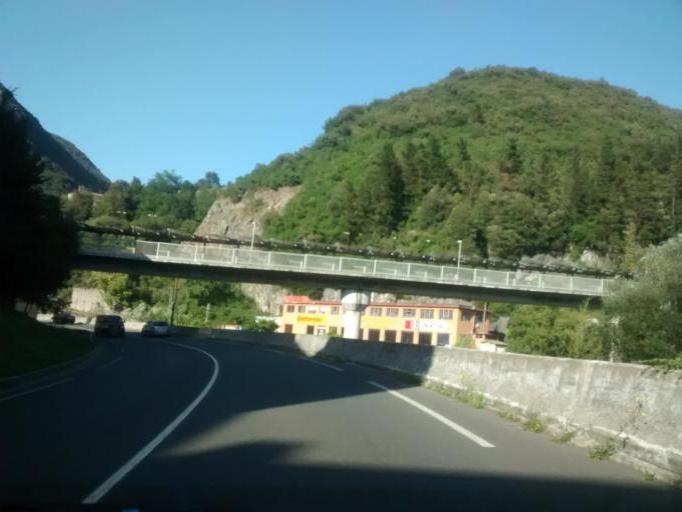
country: ES
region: Basque Country
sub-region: Provincia de Guipuzcoa
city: Mendaro
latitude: 43.2533
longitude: -2.3874
